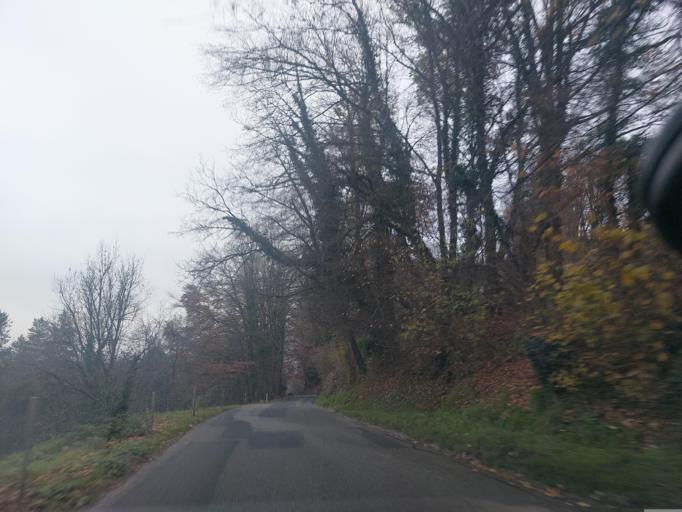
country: CH
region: Vaud
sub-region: Riviera-Pays-d'Enhaut District
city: Blonay
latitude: 46.4900
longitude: 6.8737
